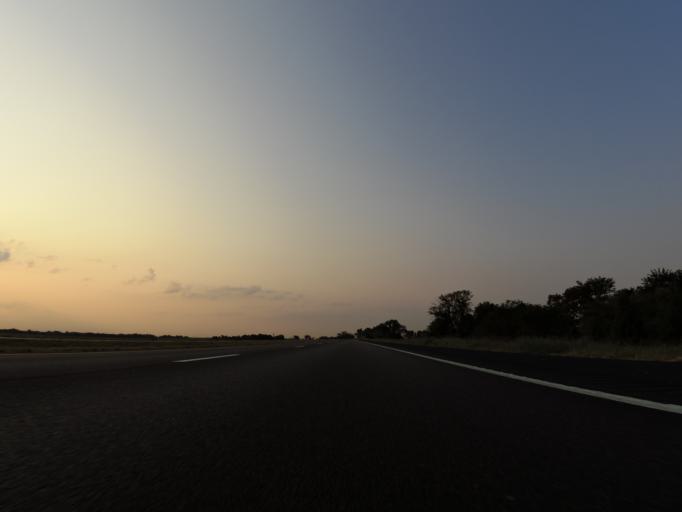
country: US
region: Kansas
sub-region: Sedgwick County
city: Maize
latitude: 37.8072
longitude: -97.4988
